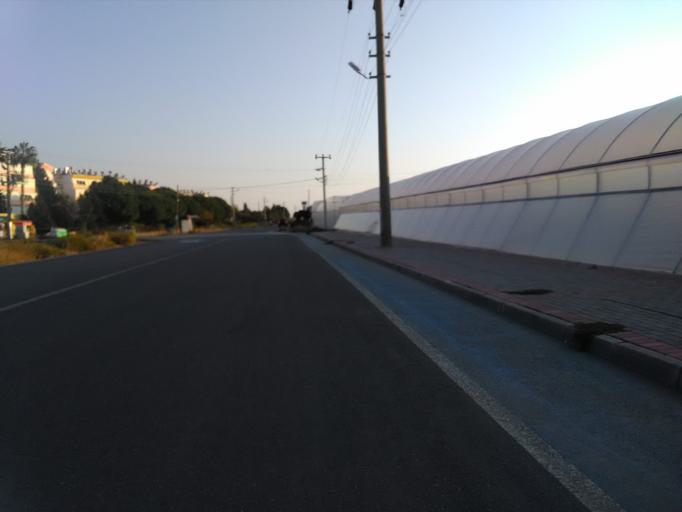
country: TR
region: Antalya
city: Gazipasa
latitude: 36.2571
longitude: 32.2904
